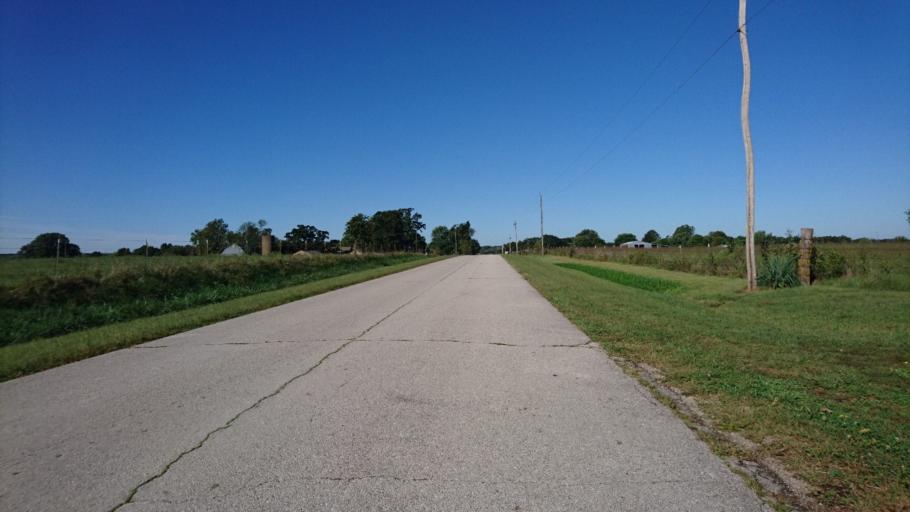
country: US
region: Missouri
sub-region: Greene County
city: Ash Grove
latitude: 37.1942
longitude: -93.6749
